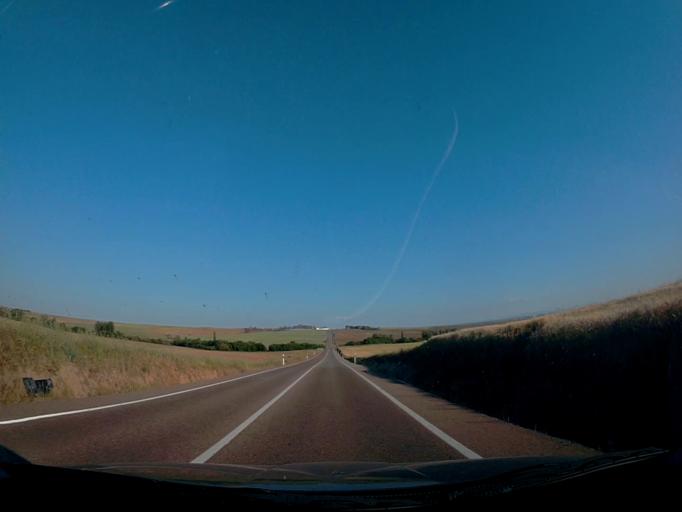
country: ES
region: Castille-La Mancha
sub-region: Province of Toledo
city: Hormigos
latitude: 40.1079
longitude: -4.3991
